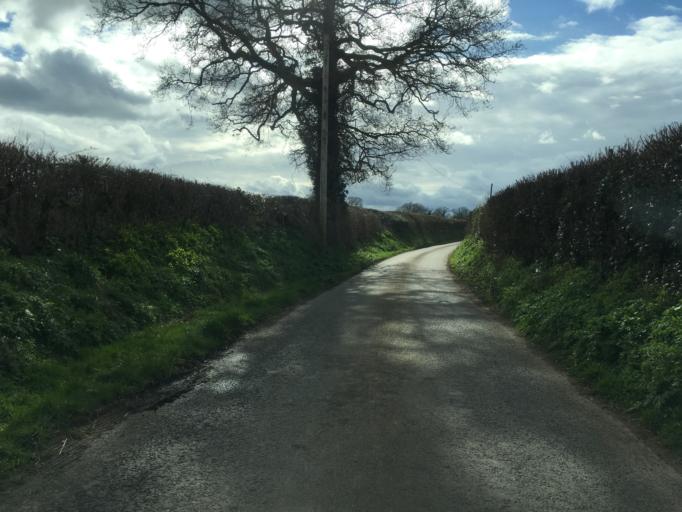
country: GB
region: England
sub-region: Gloucestershire
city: Newent
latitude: 51.8557
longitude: -2.3877
